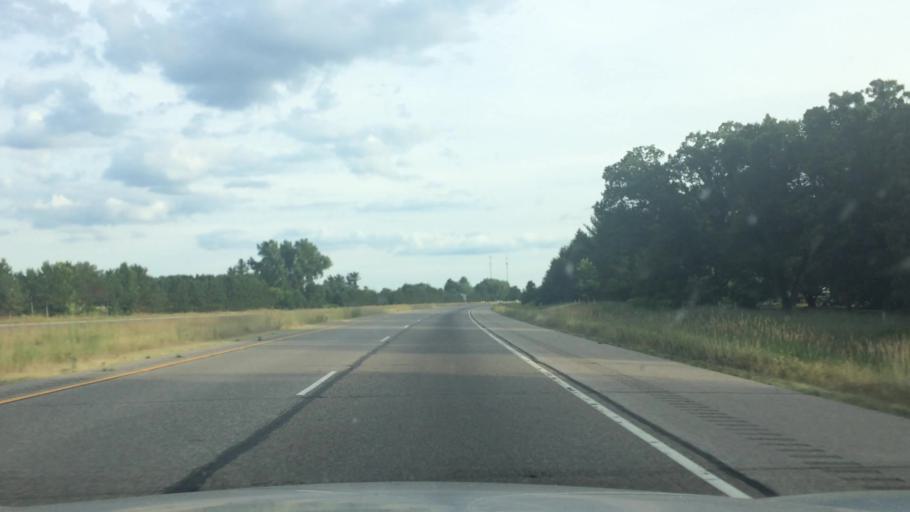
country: US
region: Wisconsin
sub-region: Portage County
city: Plover
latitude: 44.1995
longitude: -89.5230
